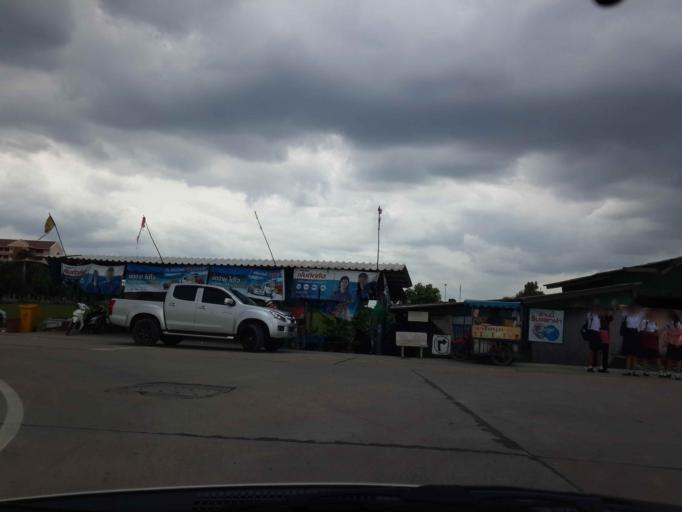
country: TH
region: Bangkok
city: Sai Mai
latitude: 13.8926
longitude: 100.6962
